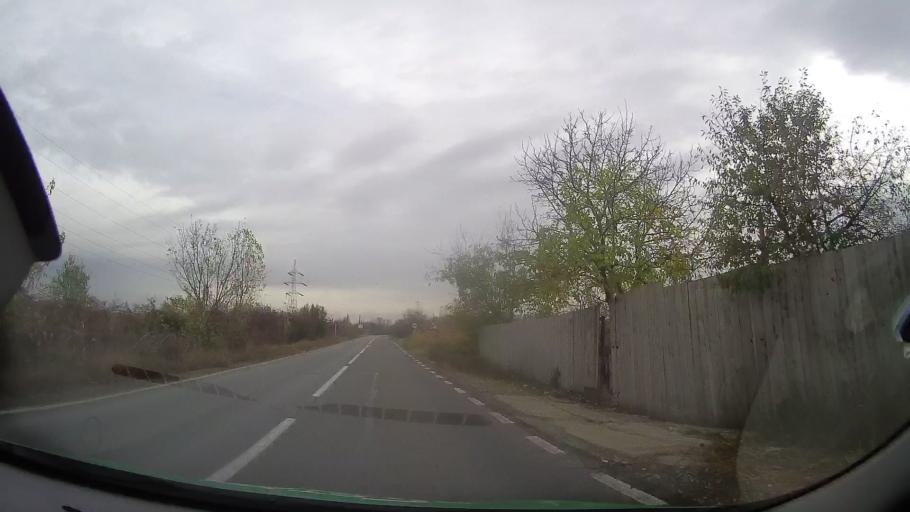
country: RO
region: Prahova
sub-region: Comuna Bucov
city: Bucov
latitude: 44.9500
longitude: 26.0954
